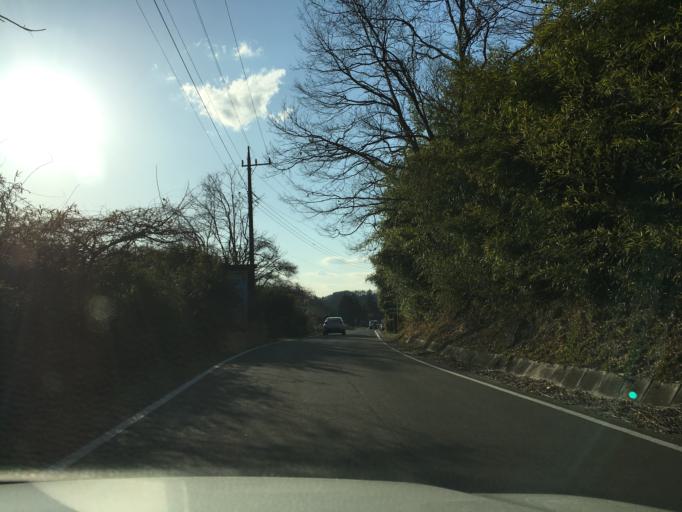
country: JP
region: Ibaraki
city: Daigo
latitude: 36.7731
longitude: 140.2533
